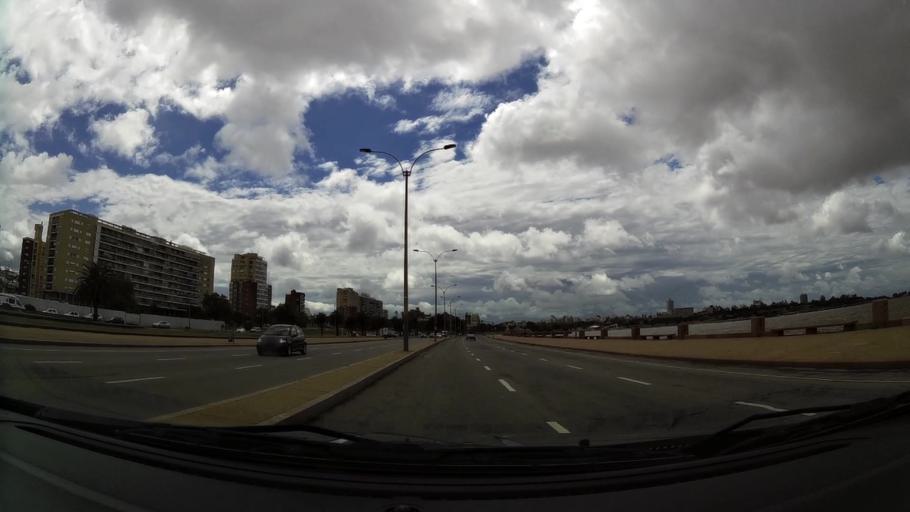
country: UY
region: Montevideo
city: Montevideo
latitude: -34.9149
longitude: -56.1819
